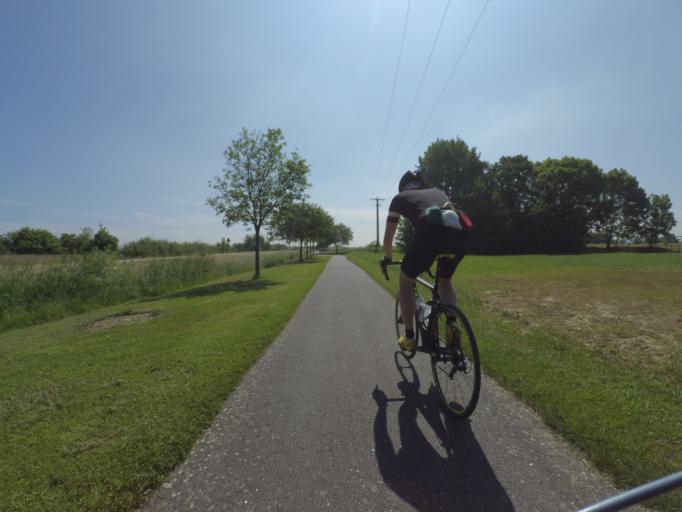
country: DE
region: Rheinland-Pfalz
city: Nortershausen
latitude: 50.2049
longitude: 7.4918
